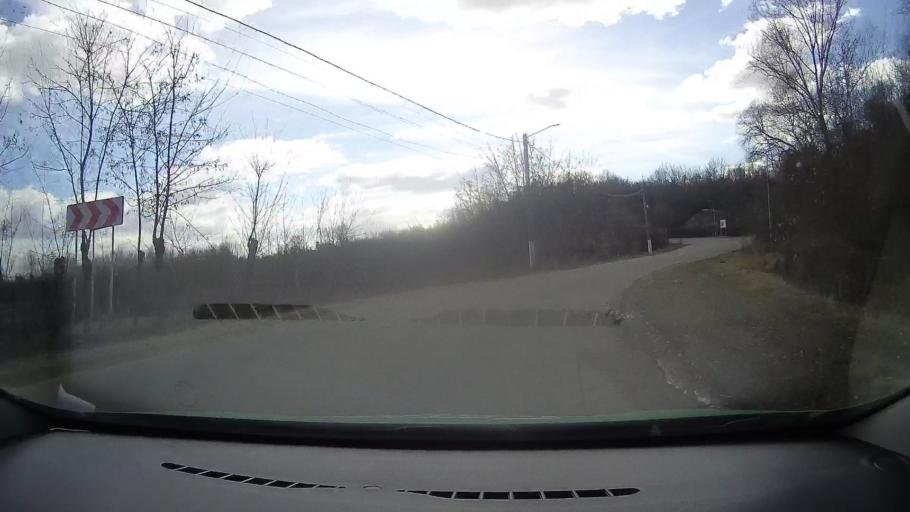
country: RO
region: Dambovita
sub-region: Comuna Sotanga
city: Teis
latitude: 44.9717
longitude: 25.3961
